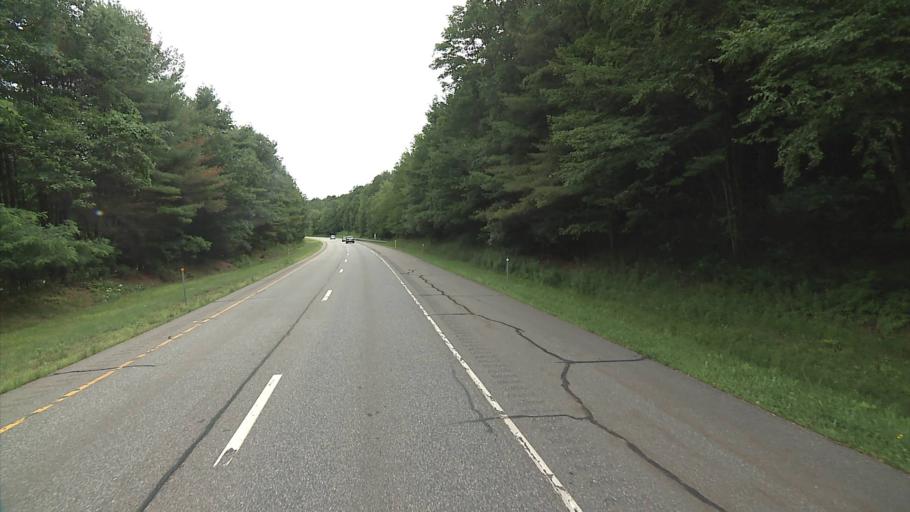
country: US
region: Connecticut
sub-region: Litchfield County
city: Winchester Center
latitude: 41.8561
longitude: -73.0865
